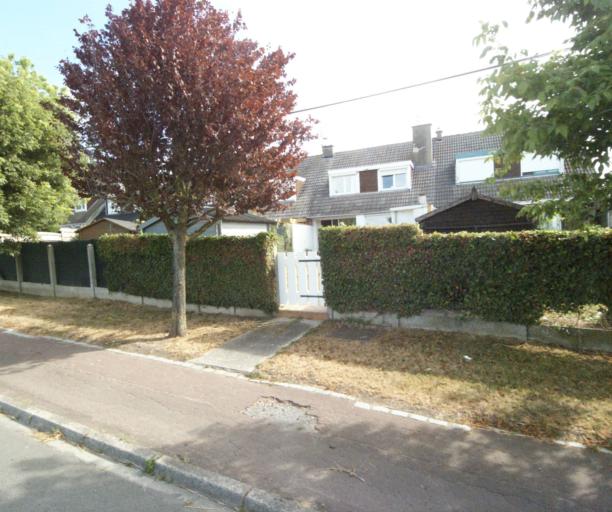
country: FR
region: Nord-Pas-de-Calais
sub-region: Departement du Nord
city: Linselles
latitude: 50.7312
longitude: 3.0796
